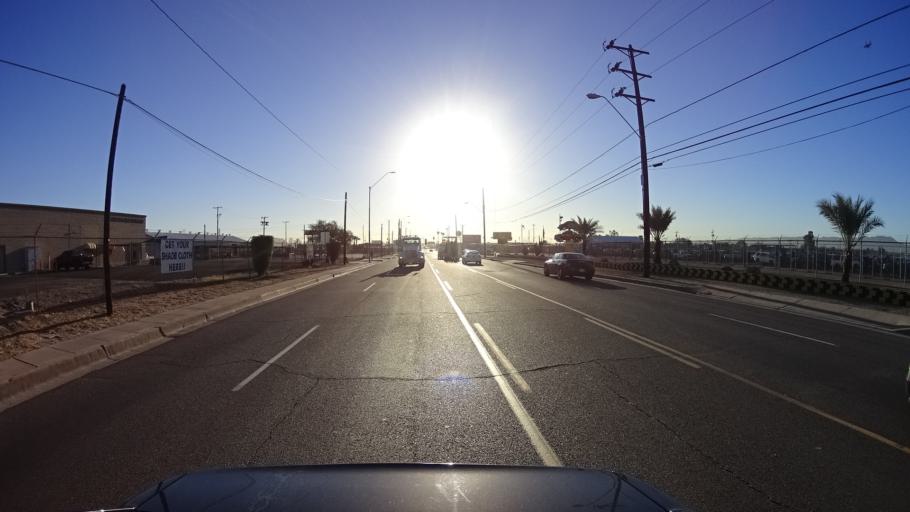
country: US
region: Arizona
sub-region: Maricopa County
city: Phoenix
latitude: 33.4368
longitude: -112.1147
